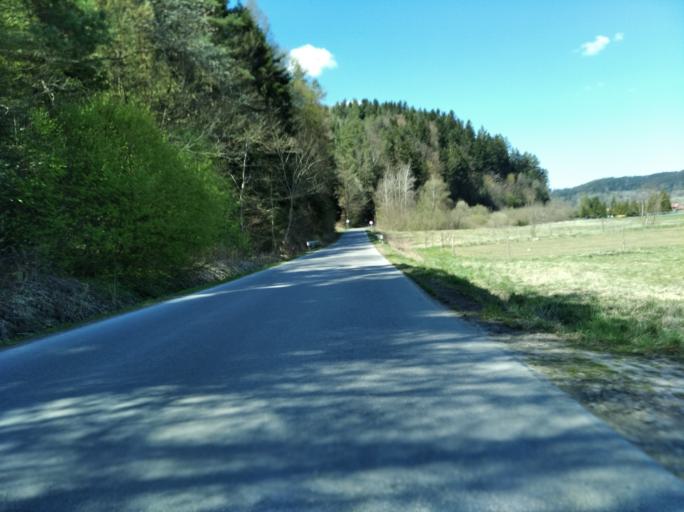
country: PL
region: Subcarpathian Voivodeship
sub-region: Powiat brzozowski
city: Dydnia
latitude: 49.6904
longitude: 22.2084
